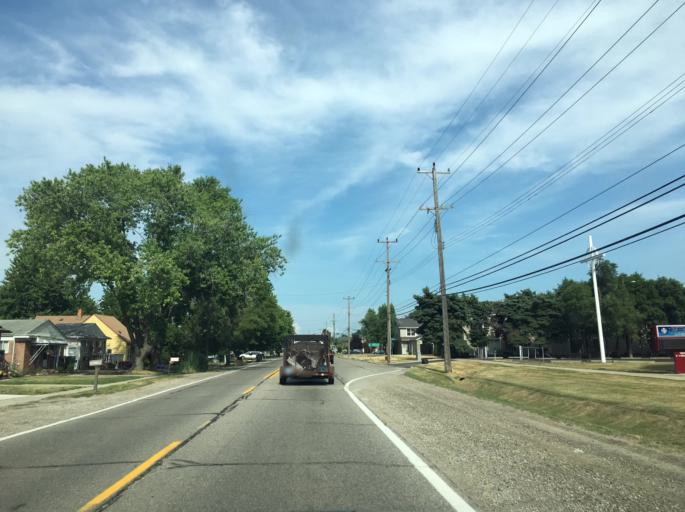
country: US
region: Michigan
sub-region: Macomb County
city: Fraser
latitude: 42.5395
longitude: -82.9221
